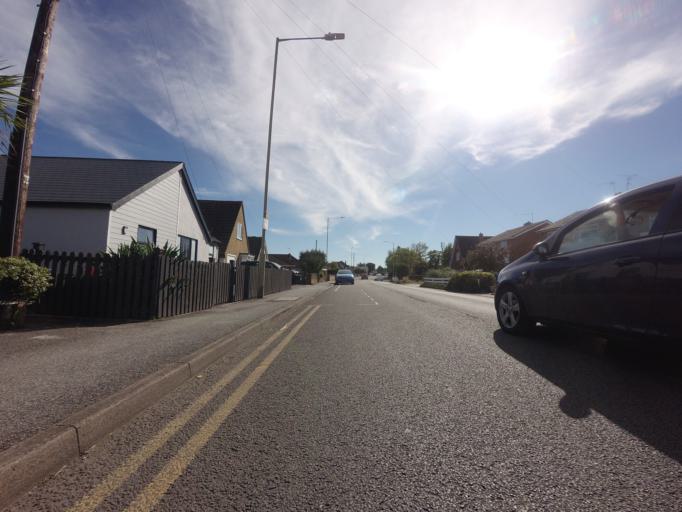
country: GB
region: England
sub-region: Kent
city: Herne Bay
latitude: 51.3693
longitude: 1.1539
